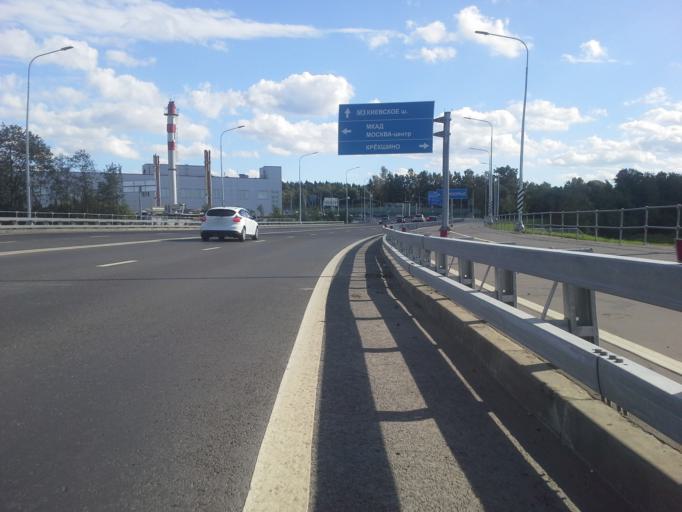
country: RU
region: Moskovskaya
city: Kokoshkino
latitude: 55.5820
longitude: 37.1637
